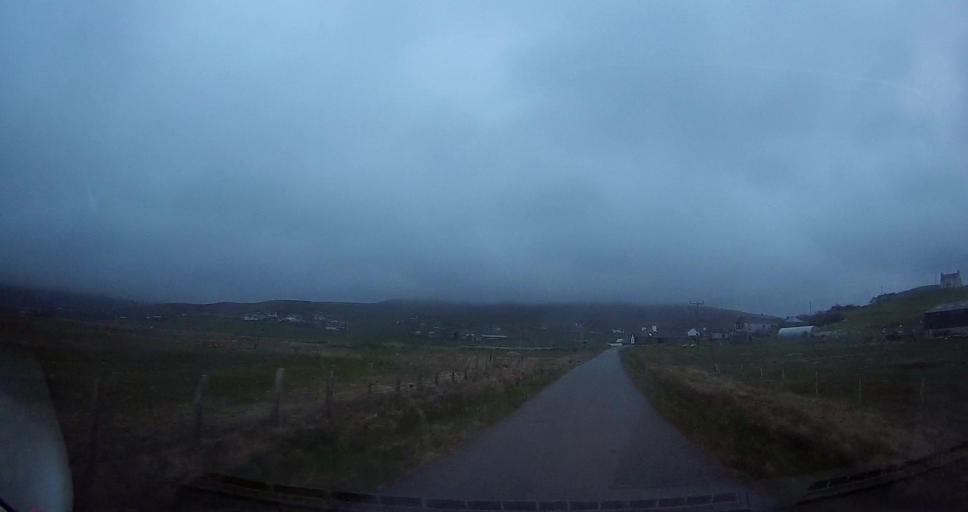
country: GB
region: Scotland
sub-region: Shetland Islands
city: Sandwick
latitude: 60.0469
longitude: -1.2117
